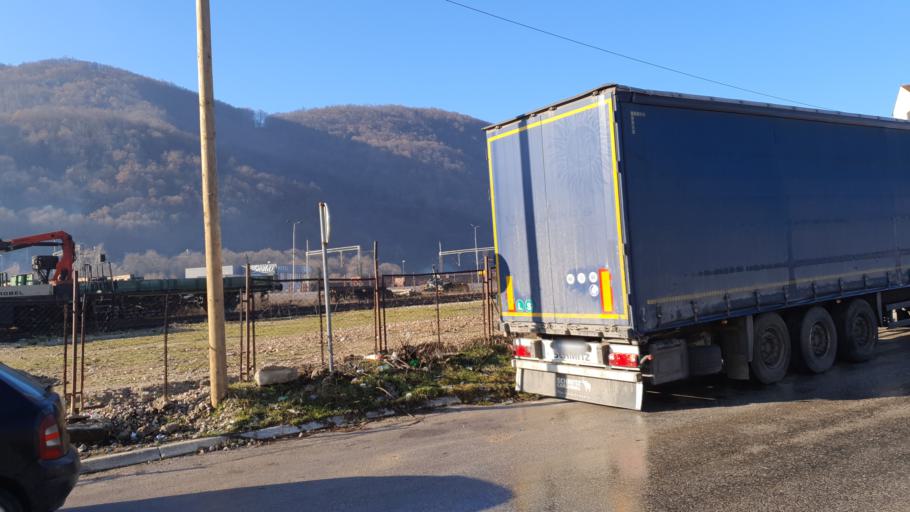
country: RS
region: Central Serbia
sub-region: Zlatiborski Okrug
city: Uzice
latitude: 43.8481
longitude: 19.8580
